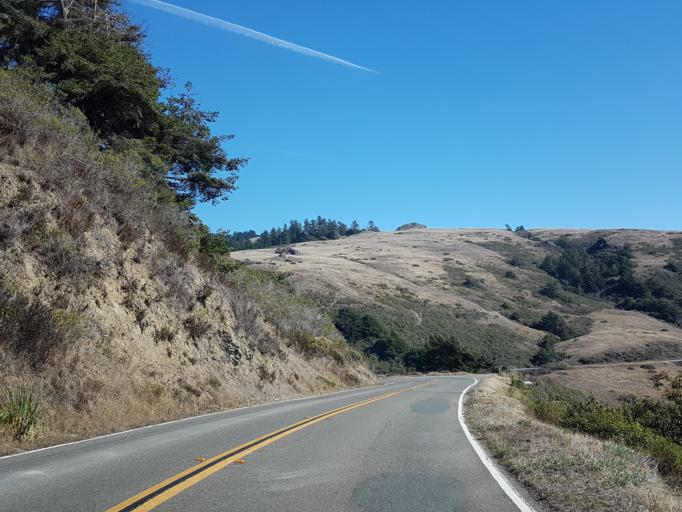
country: US
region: California
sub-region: Sonoma County
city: Monte Rio
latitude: 38.4749
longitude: -123.1558
